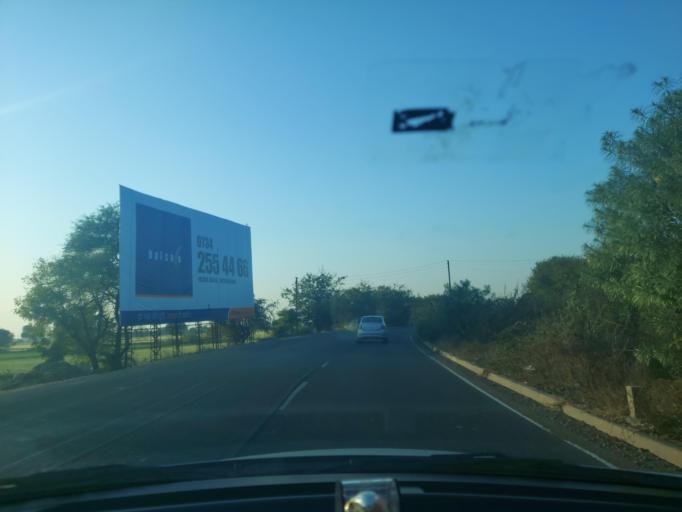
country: IN
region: Madhya Pradesh
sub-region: Ujjain
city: Ujjain
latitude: 23.0985
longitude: 75.8109
